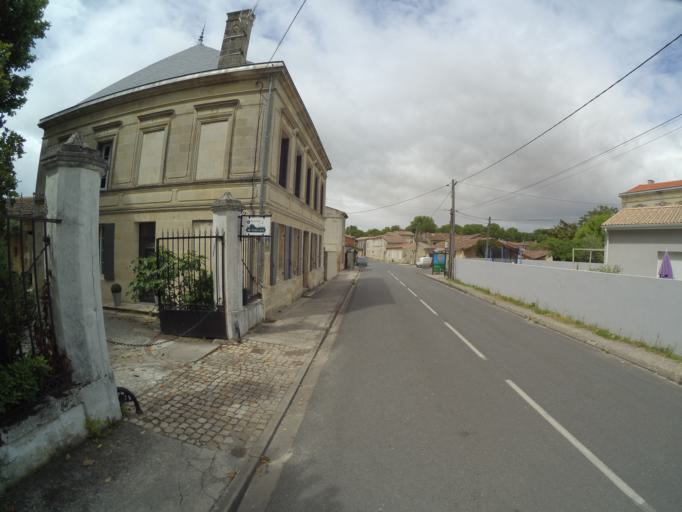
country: FR
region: Aquitaine
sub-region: Departement de la Gironde
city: Lamarque
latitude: 45.0950
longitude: -0.7204
